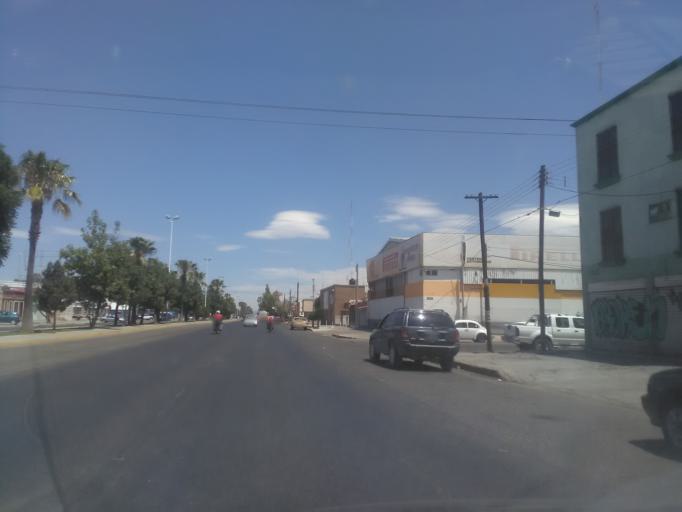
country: MX
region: Durango
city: Victoria de Durango
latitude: 24.0317
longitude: -104.6259
